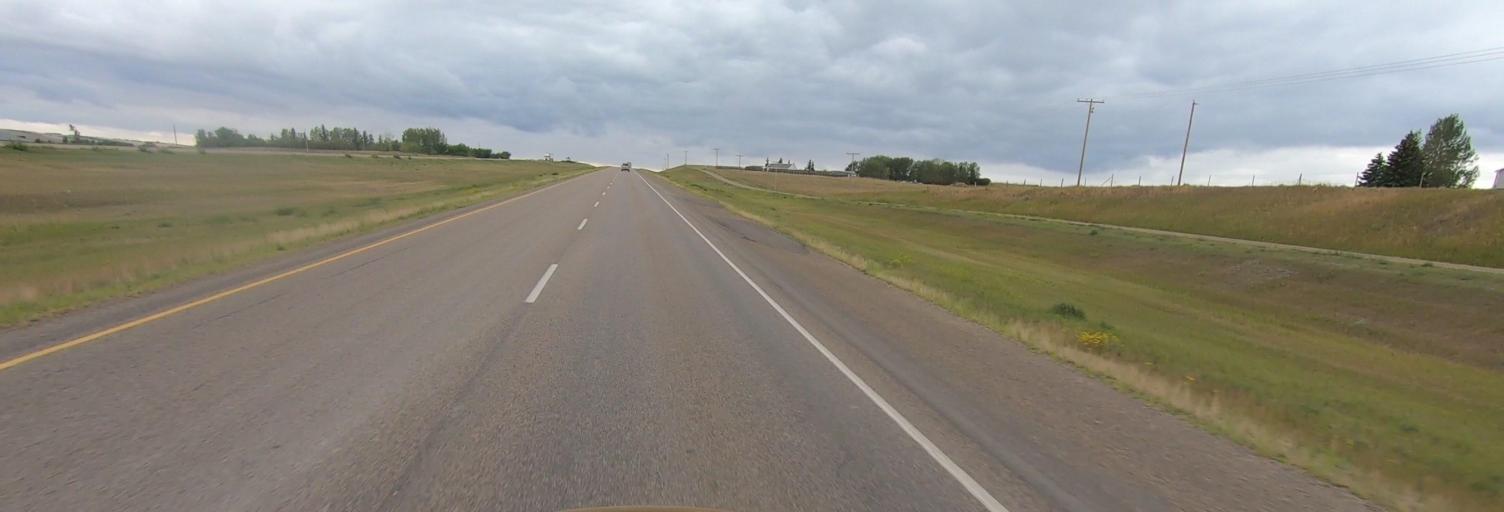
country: CA
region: Saskatchewan
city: Swift Current
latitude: 50.2756
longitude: -107.9769
